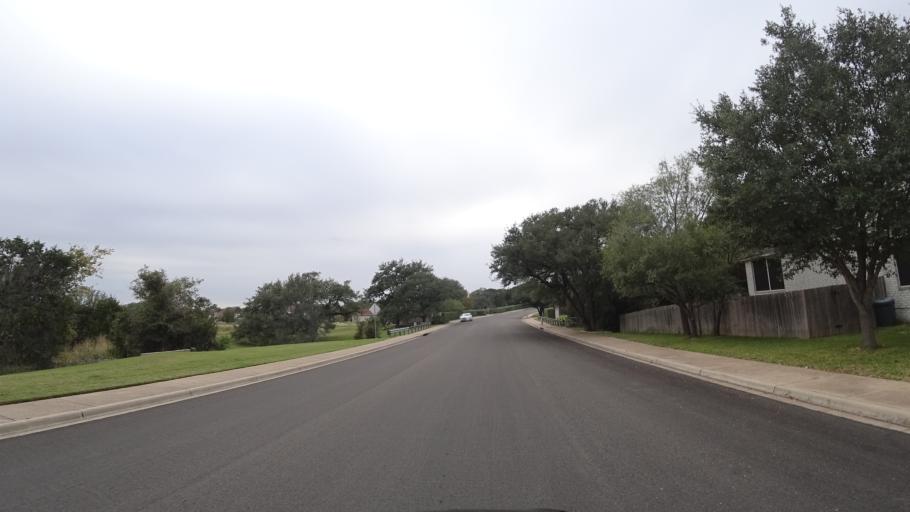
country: US
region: Texas
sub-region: Travis County
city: Shady Hollow
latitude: 30.1817
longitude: -97.8888
